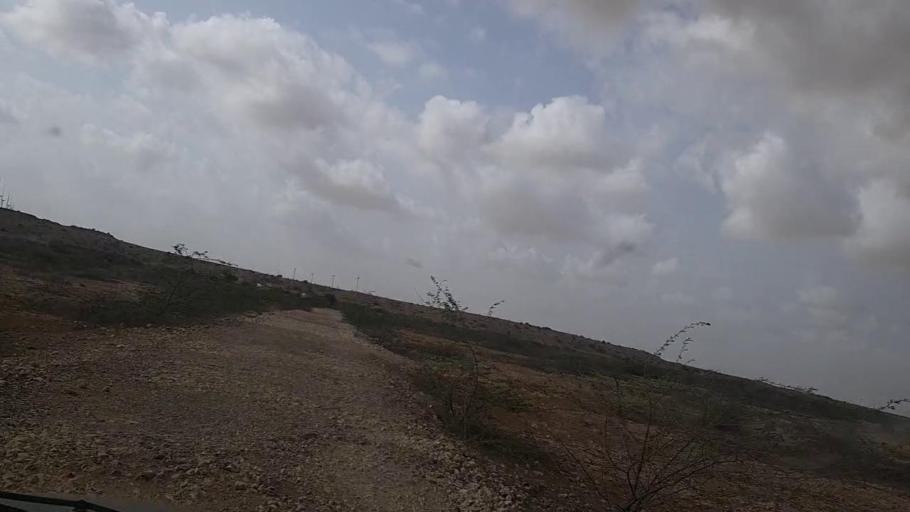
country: PK
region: Sindh
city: Thatta
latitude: 24.9235
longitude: 67.8932
